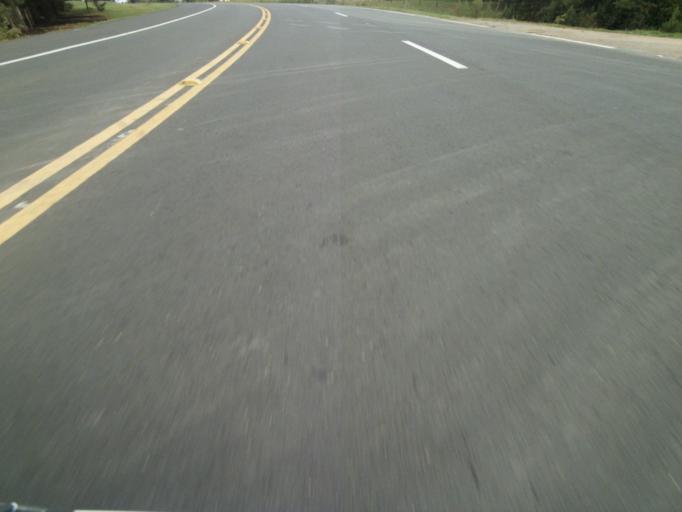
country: BR
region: Parana
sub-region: Campo Largo
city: Campo Largo
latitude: -25.4659
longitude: -49.7259
